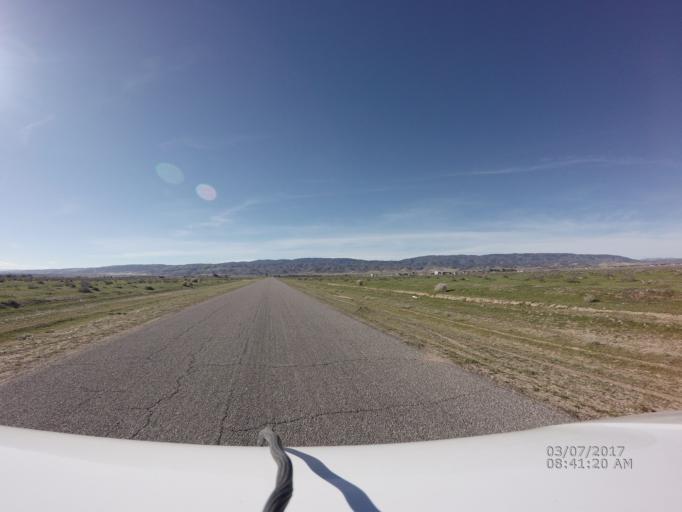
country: US
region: California
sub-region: Los Angeles County
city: Green Valley
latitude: 34.7956
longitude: -118.5457
